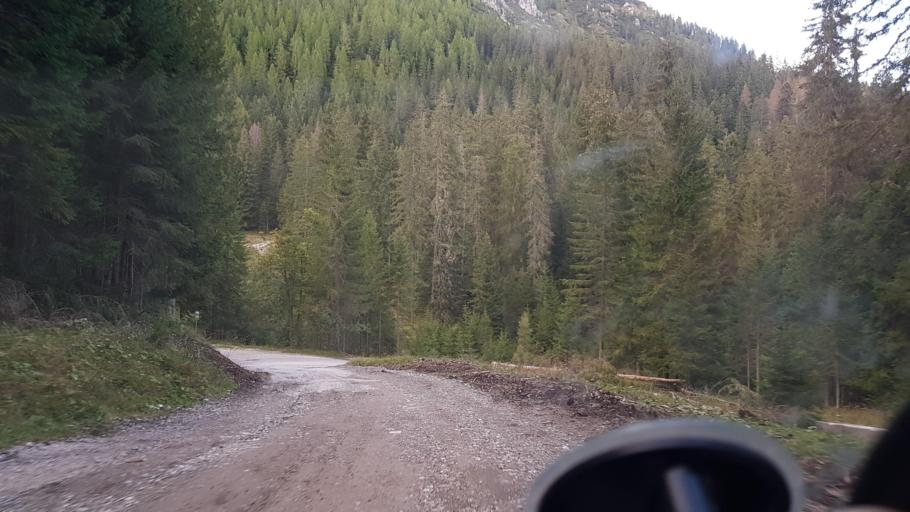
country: IT
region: Veneto
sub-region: Provincia di Belluno
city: San Pietro di Cadore
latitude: 46.6084
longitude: 12.5959
